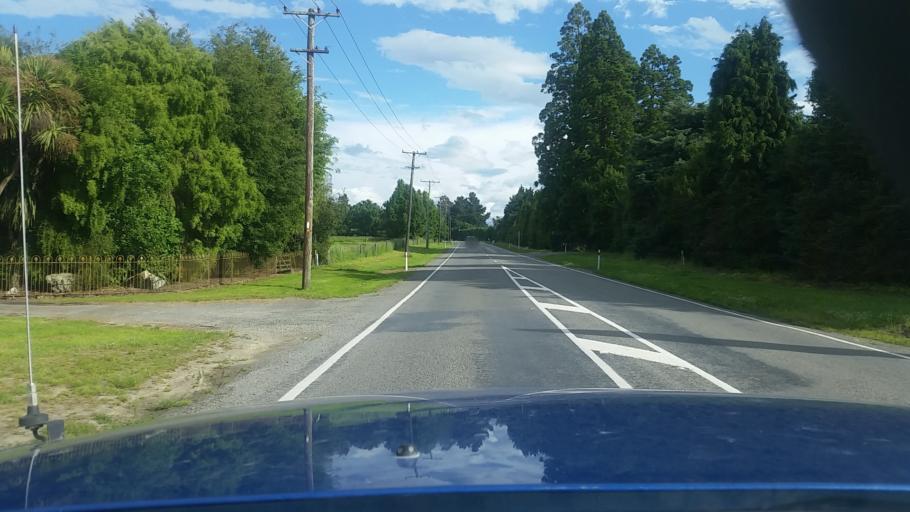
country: NZ
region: Canterbury
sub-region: Ashburton District
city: Ashburton
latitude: -43.8809
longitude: 171.7315
